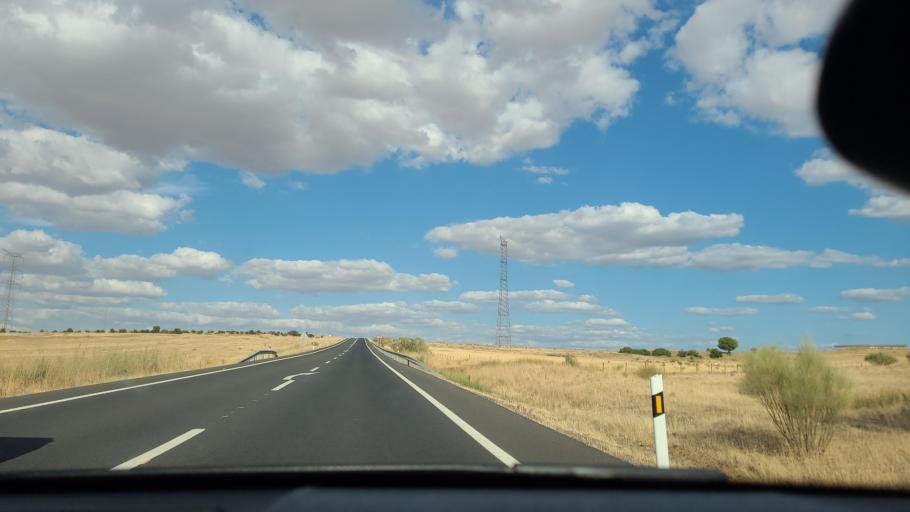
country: ES
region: Extremadura
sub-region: Provincia de Badajoz
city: Ahillones
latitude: 38.2545
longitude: -5.9090
